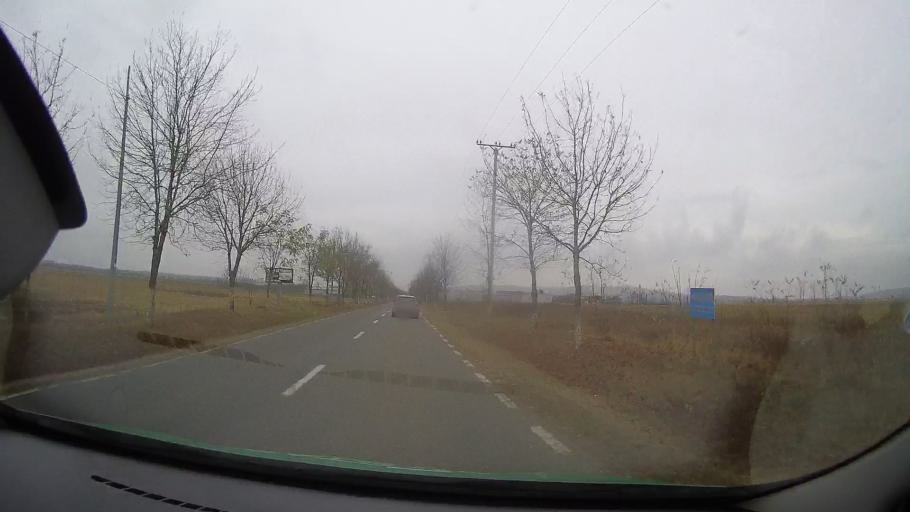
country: RO
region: Prahova
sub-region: Oras Baicoi
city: Liliesti
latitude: 45.0126
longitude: 25.8847
